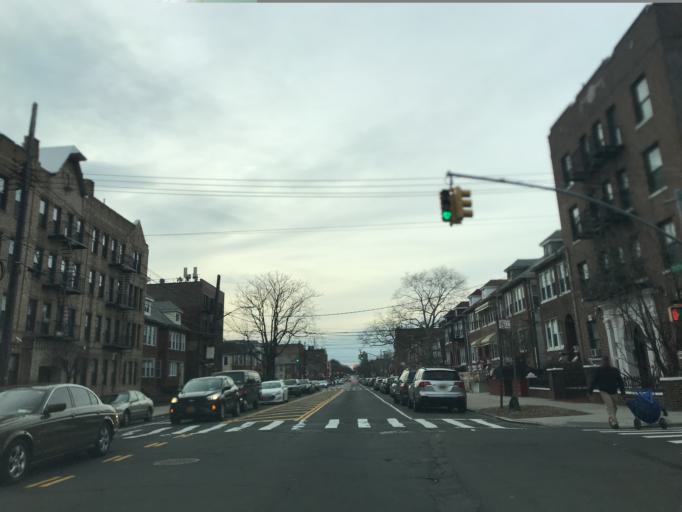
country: US
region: New York
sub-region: Kings County
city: Brooklyn
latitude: 40.6541
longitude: -73.9265
